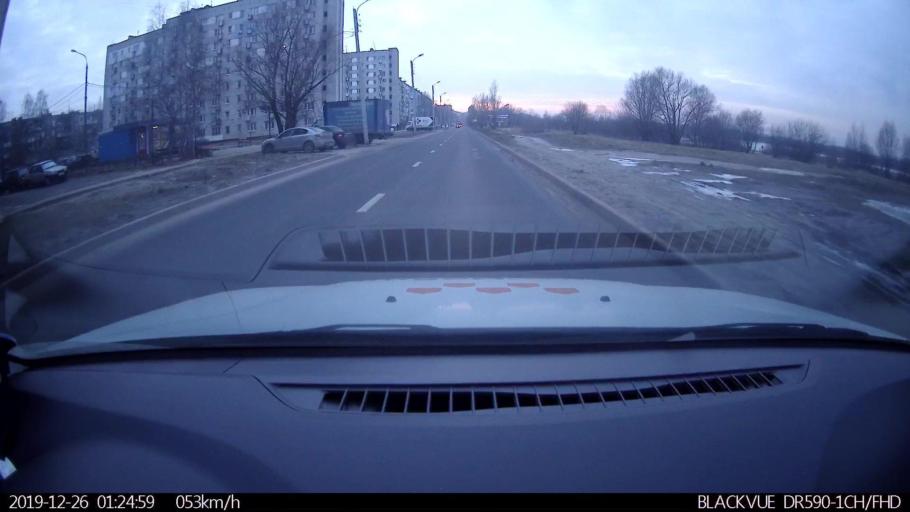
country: RU
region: Nizjnij Novgorod
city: Gorbatovka
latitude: 56.2698
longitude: 43.8716
